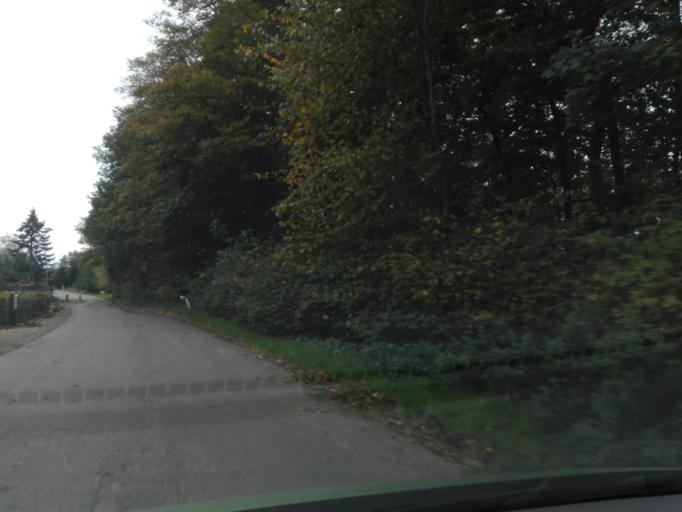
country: DK
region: Central Jutland
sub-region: Arhus Kommune
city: Tranbjerg
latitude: 56.0648
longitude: 10.1131
